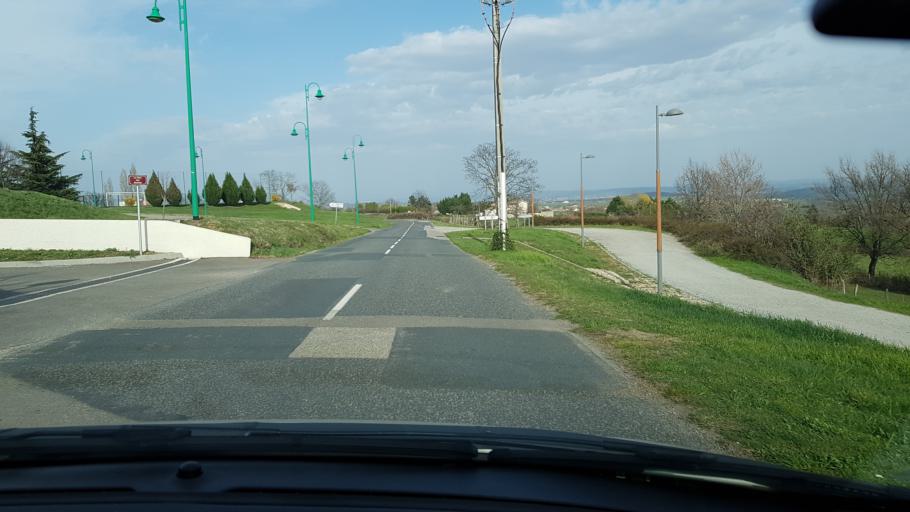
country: FR
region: Rhone-Alpes
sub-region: Departement du Rhone
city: Saint-Maurice-sur-Dargoire
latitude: 45.5854
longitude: 4.6398
